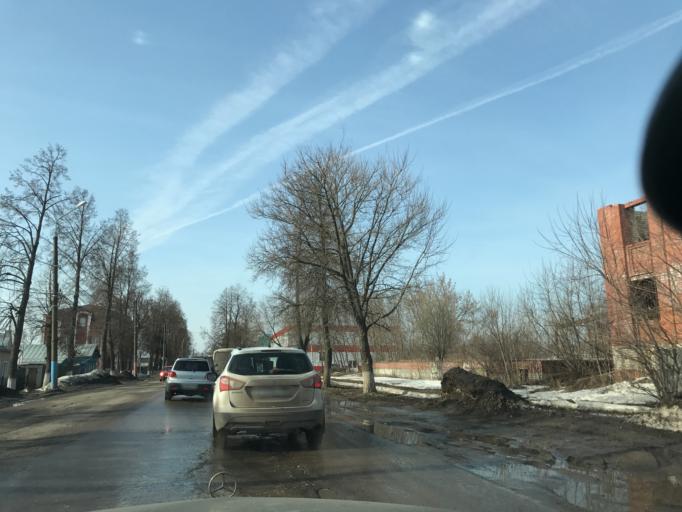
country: RU
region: Nizjnij Novgorod
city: Pavlovo
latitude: 55.9624
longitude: 43.0903
